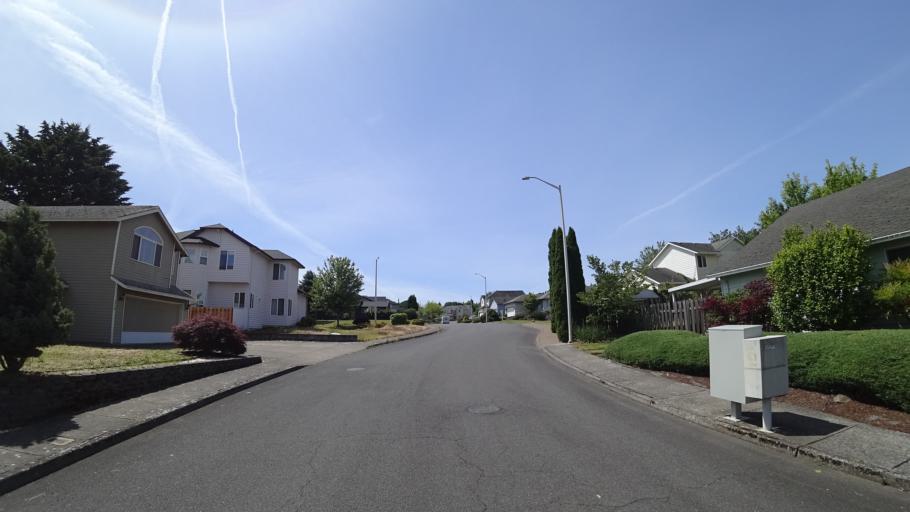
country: US
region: Oregon
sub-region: Multnomah County
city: Fairview
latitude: 45.5509
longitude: -122.5083
